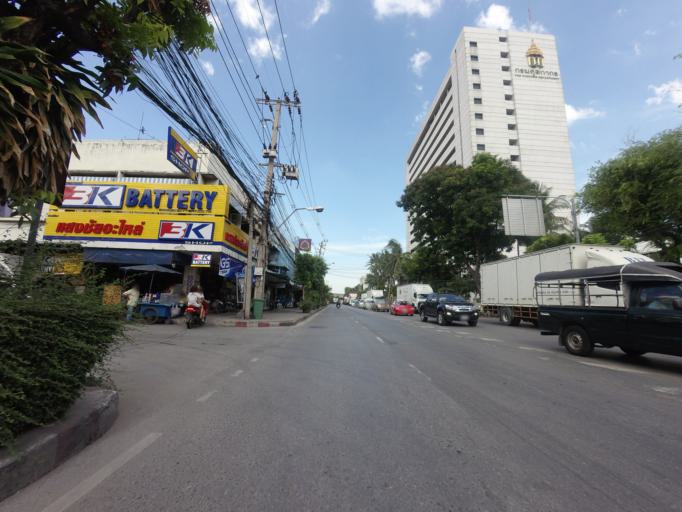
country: TH
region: Bangkok
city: Khlong Toei
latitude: 13.7139
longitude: 100.5669
